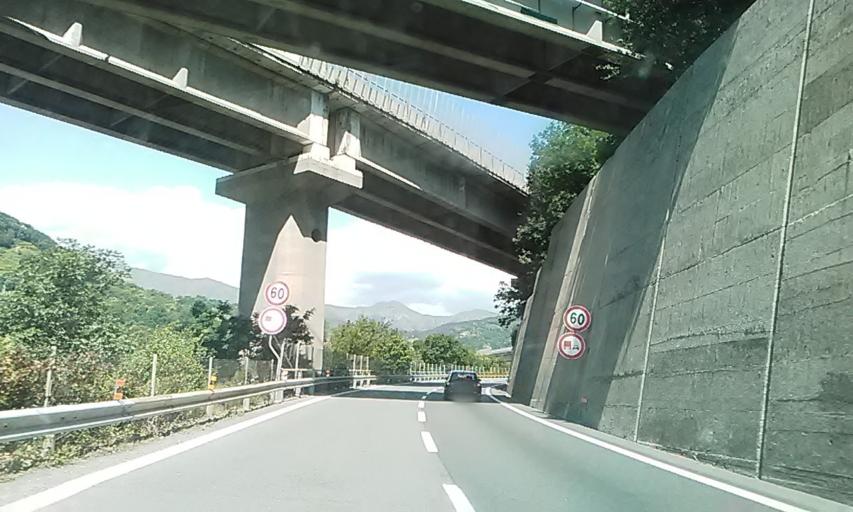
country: IT
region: Liguria
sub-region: Provincia di Genova
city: Mele
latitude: 44.4318
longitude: 8.7415
